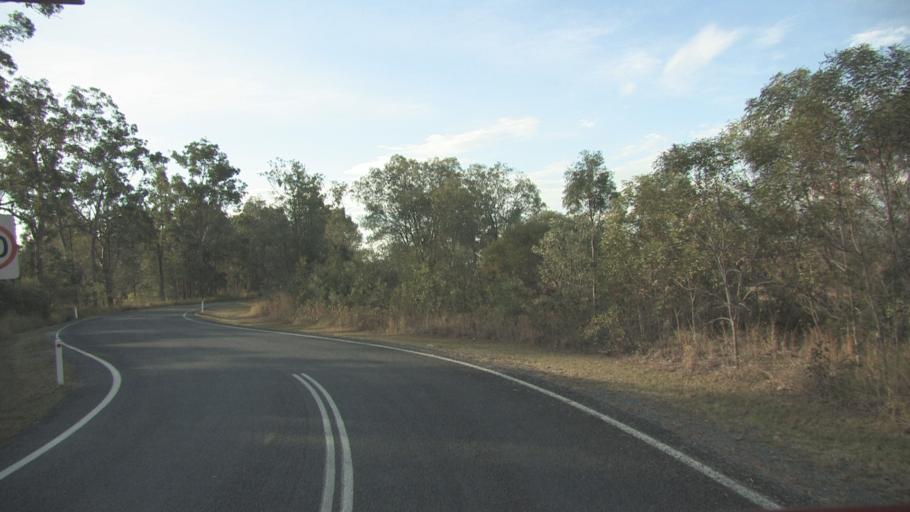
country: AU
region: Queensland
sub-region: Logan
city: Cedar Vale
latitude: -27.8444
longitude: 153.1193
